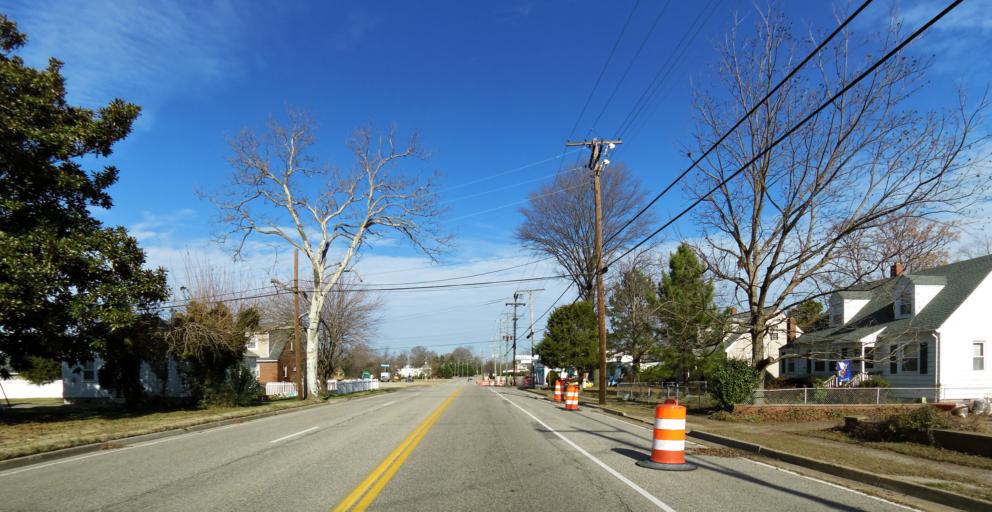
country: US
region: Virginia
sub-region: City of Hampton
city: Hampton
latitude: 37.0156
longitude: -76.3529
